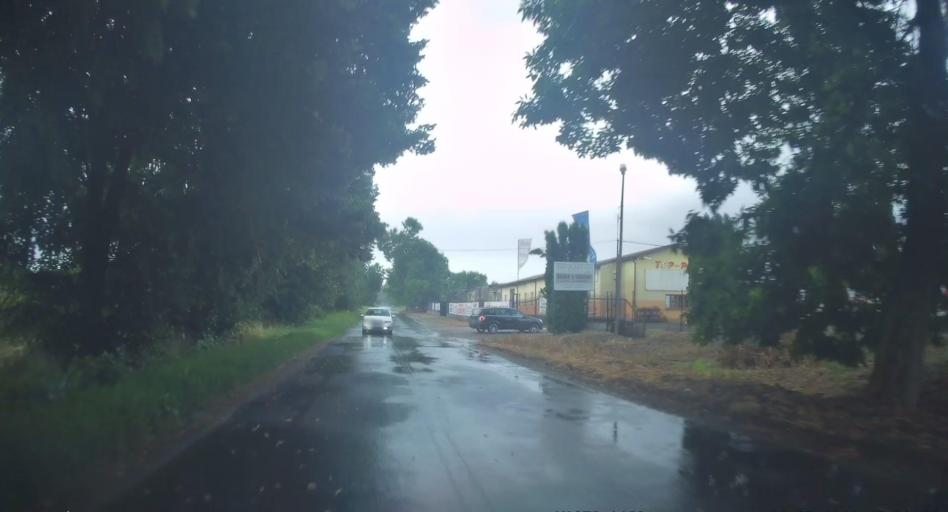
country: PL
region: Lodz Voivodeship
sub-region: Powiat brzezinski
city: Rogow
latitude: 51.8094
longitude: 19.8748
